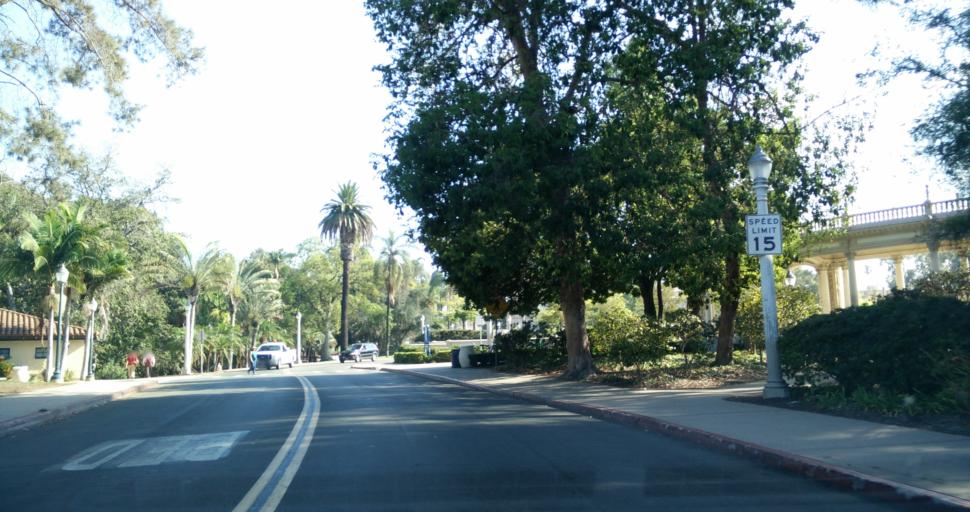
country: US
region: California
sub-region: San Diego County
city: San Diego
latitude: 32.7293
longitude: -117.1512
